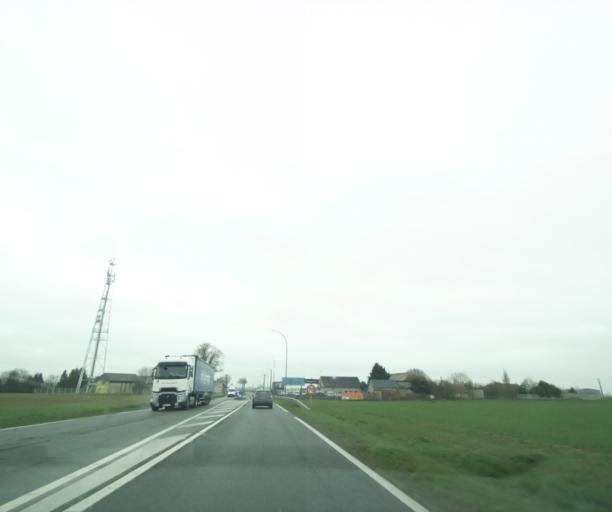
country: FR
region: Centre
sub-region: Departement d'Eure-et-Loir
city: Toury
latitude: 48.2296
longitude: 1.9517
